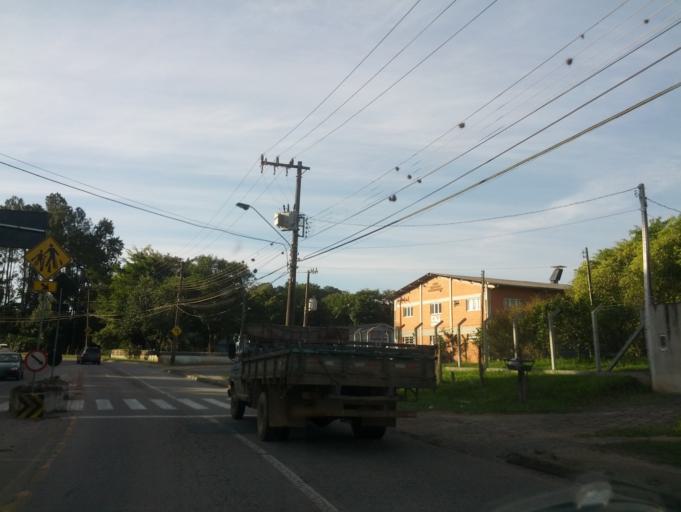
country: BR
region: Santa Catarina
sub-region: Indaial
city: Indaial
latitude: -26.8997
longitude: -49.1489
